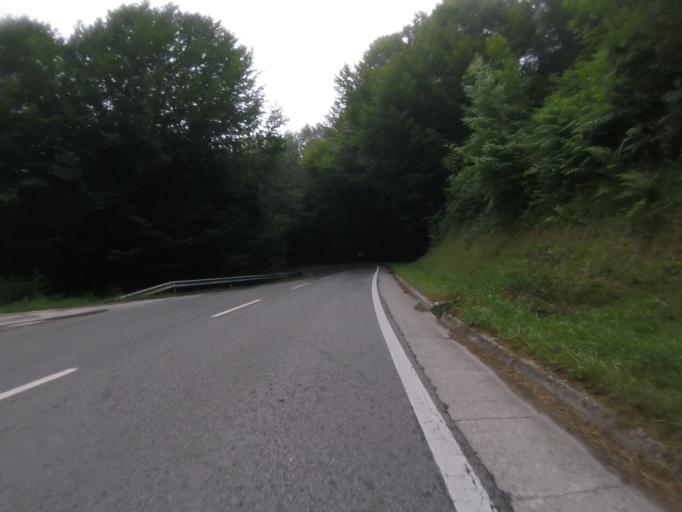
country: ES
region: Navarre
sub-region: Provincia de Navarra
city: Leitza
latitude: 43.0839
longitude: -1.8724
